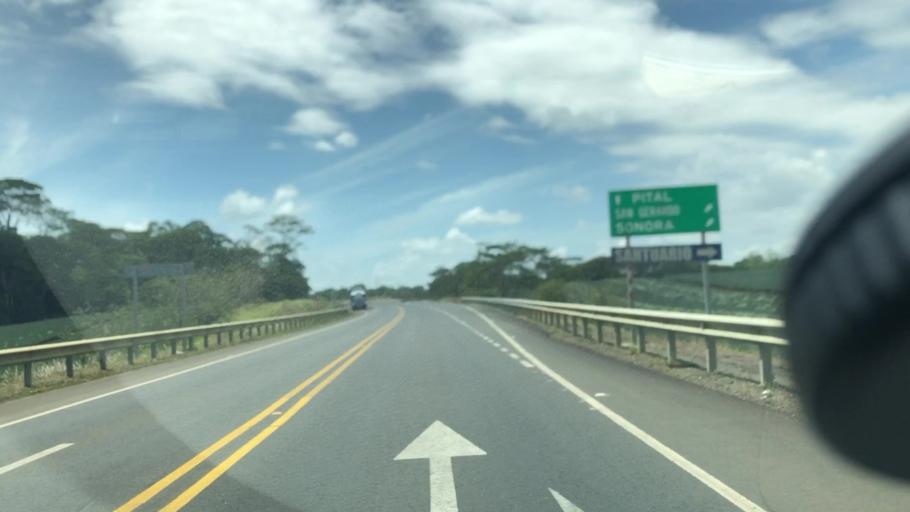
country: CR
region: Heredia
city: La Virgen
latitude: 10.4408
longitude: -84.1553
